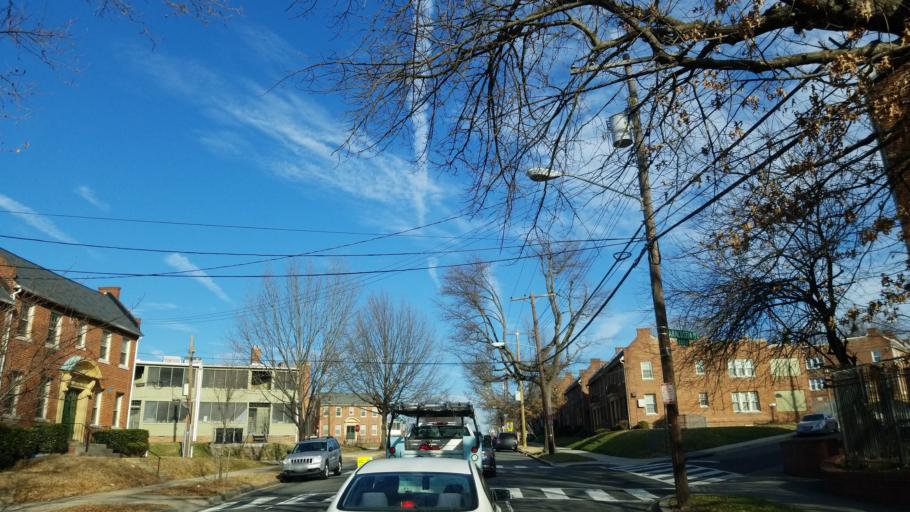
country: US
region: Maryland
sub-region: Prince George's County
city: Silver Hill
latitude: 38.8750
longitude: -76.9676
